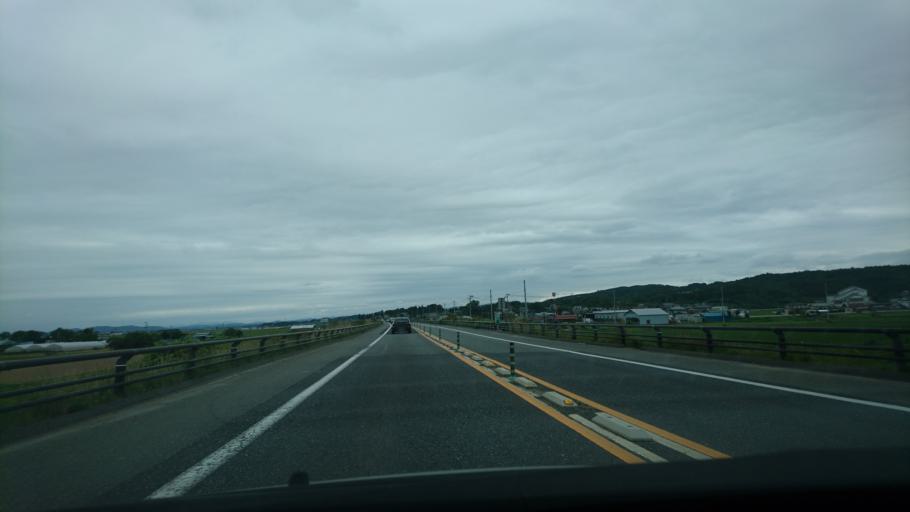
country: JP
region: Miyagi
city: Wakuya
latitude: 38.6582
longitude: 141.2648
